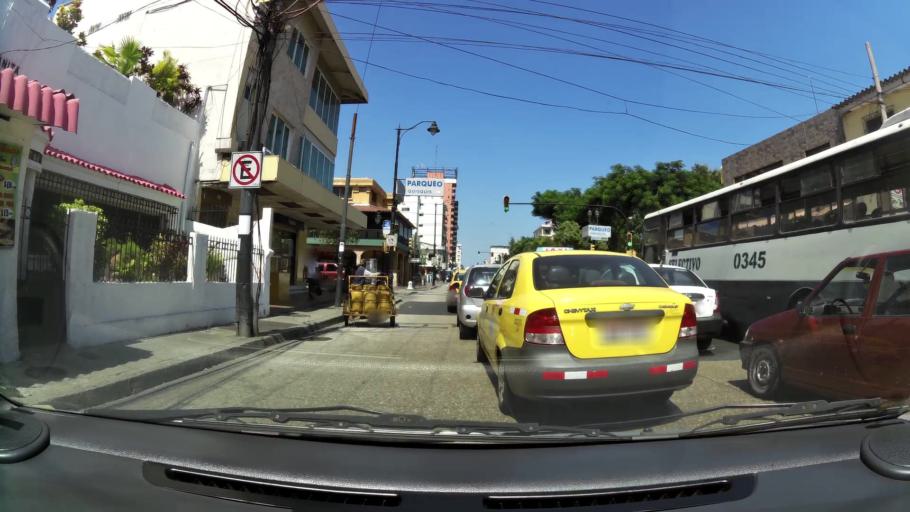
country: EC
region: Guayas
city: Guayaquil
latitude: -2.1857
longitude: -79.8957
